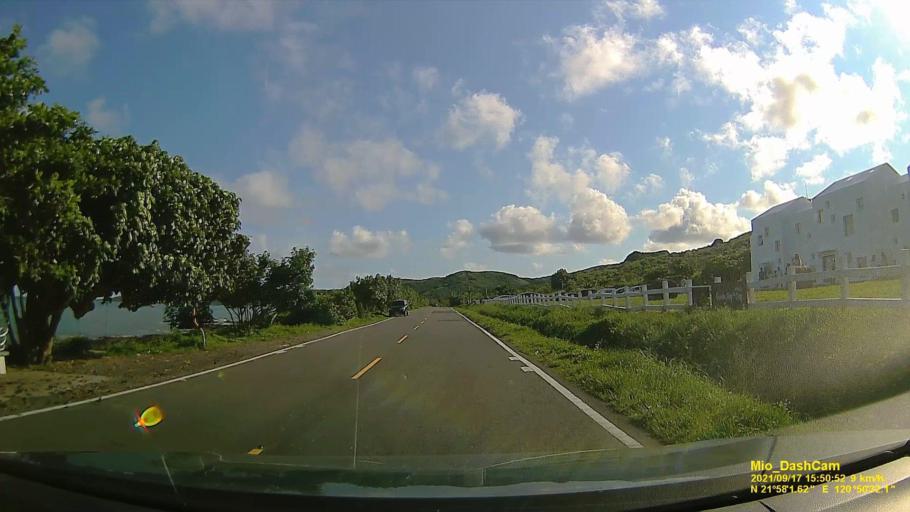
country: TW
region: Taiwan
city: Hengchun
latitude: 21.9671
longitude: 120.8422
